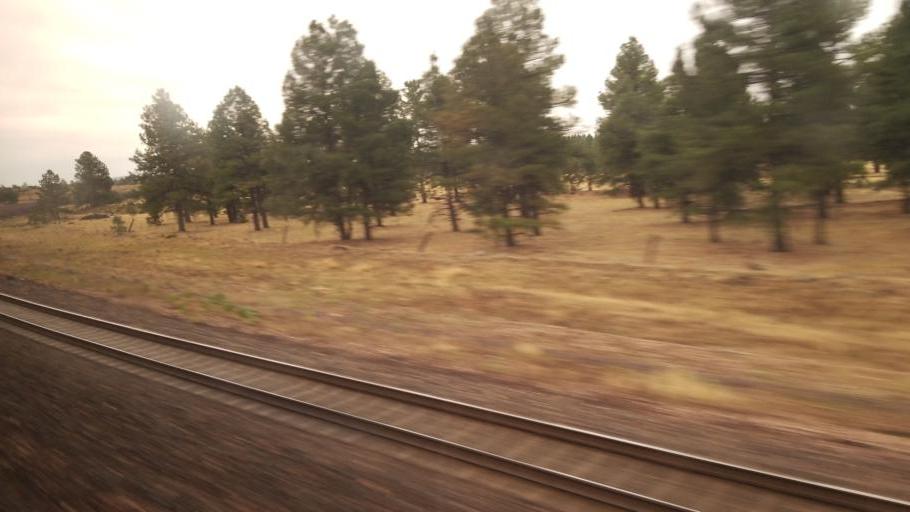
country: US
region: Arizona
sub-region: Coconino County
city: Parks
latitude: 35.2415
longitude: -111.9912
